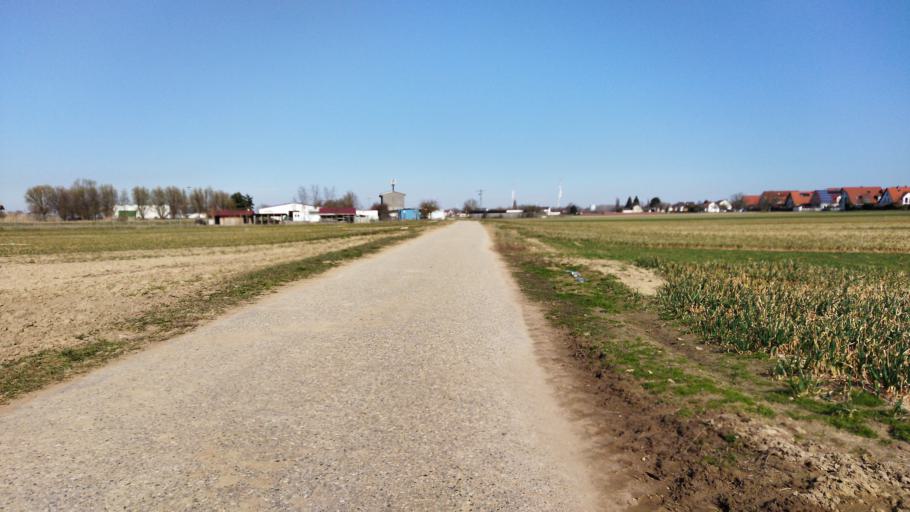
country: DE
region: Rheinland-Pfalz
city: Otterstadt
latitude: 49.3702
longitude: 8.4422
